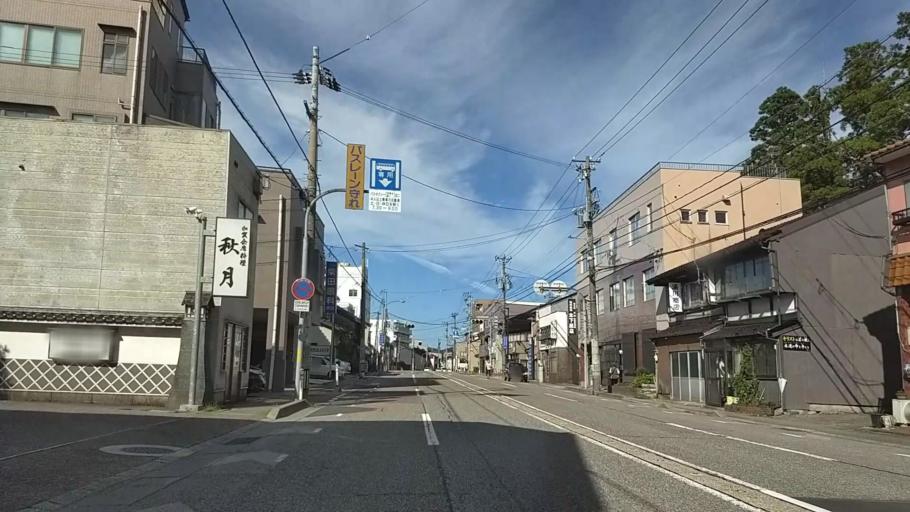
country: JP
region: Ishikawa
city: Kanazawa-shi
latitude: 36.5761
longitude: 136.6675
